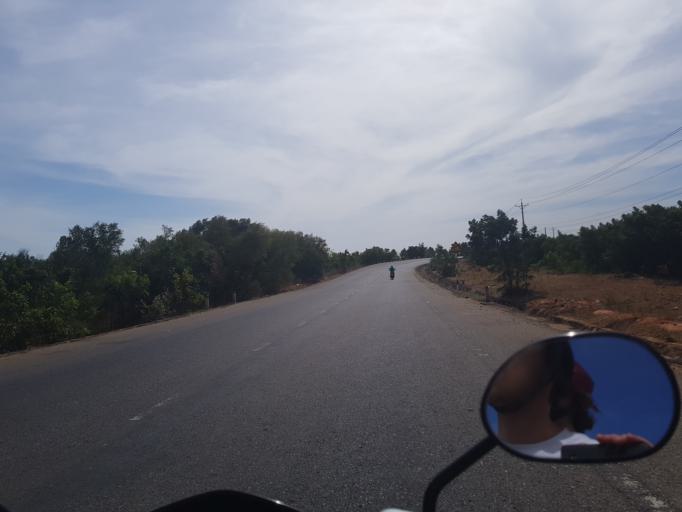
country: VN
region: Binh Thuan
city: Cho Lau
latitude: 11.0460
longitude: 108.3762
